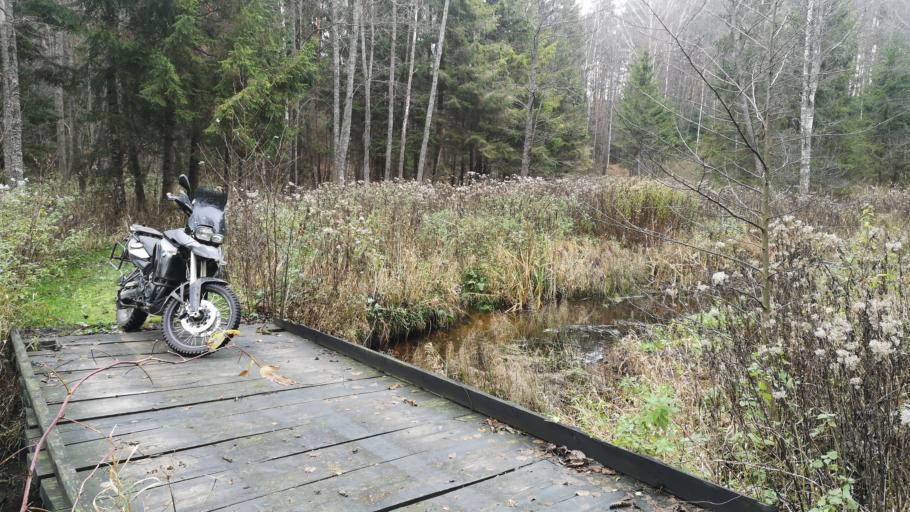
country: LT
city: Kazlu Ruda
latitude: 54.8642
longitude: 23.4655
